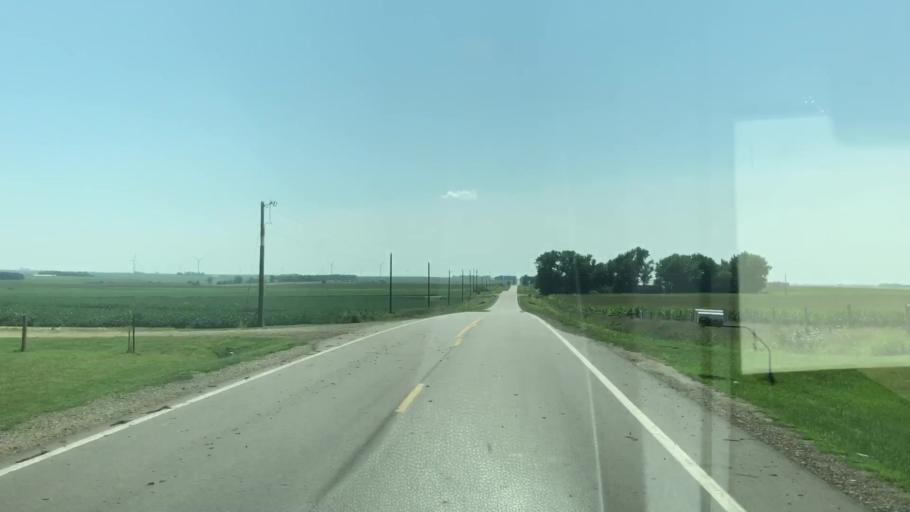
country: US
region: Iowa
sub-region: O'Brien County
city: Sanborn
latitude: 43.2615
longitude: -95.7236
